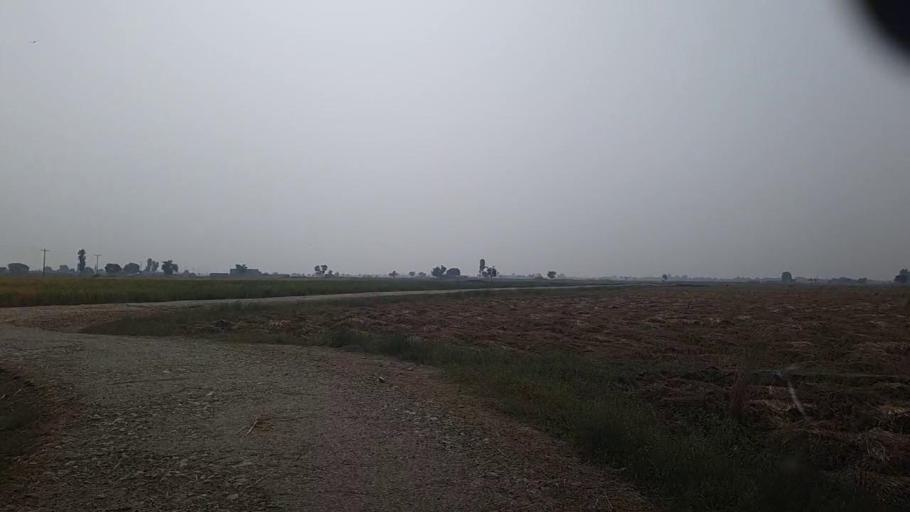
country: PK
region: Sindh
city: Kashmor
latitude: 28.3849
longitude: 69.4301
